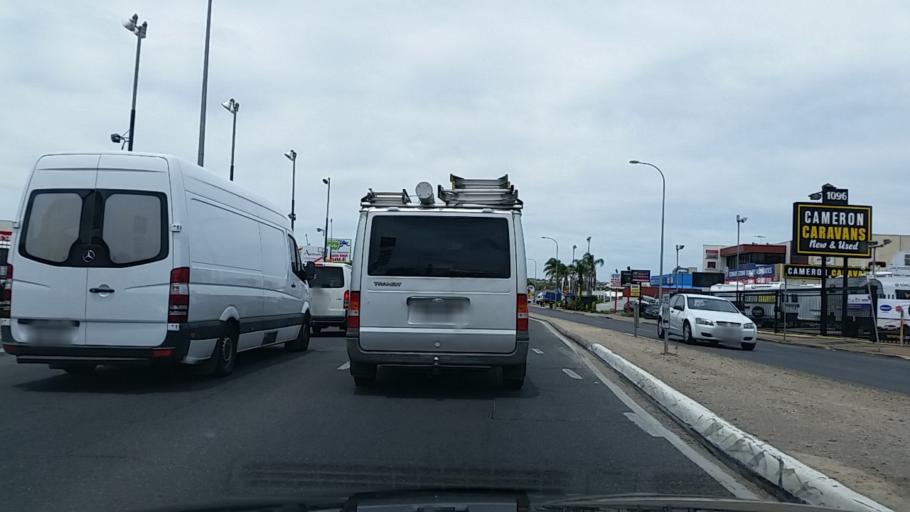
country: AU
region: South Australia
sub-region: Marion
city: Clovelly Park
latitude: -34.9908
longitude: 138.5747
